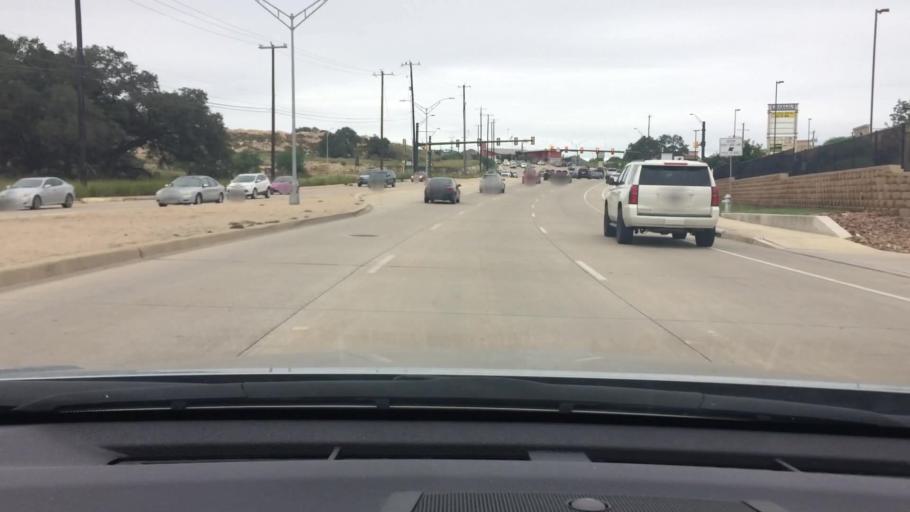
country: US
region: Texas
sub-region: Bexar County
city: Hollywood Park
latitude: 29.6034
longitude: -98.4187
